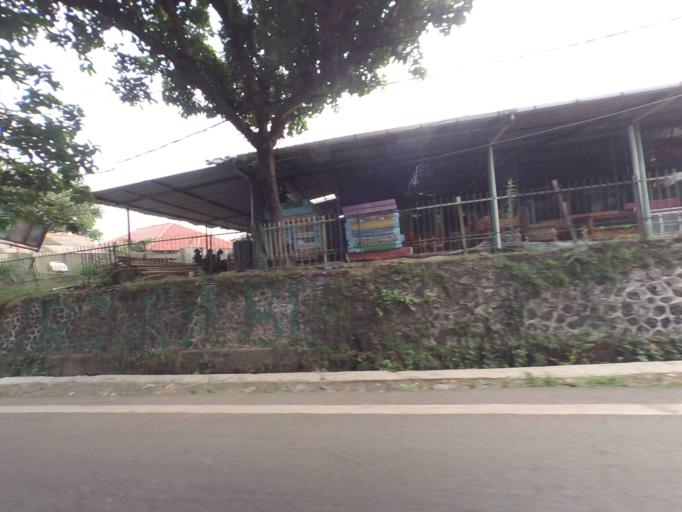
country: ID
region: West Java
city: Ciampea
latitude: -6.5549
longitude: 106.6993
